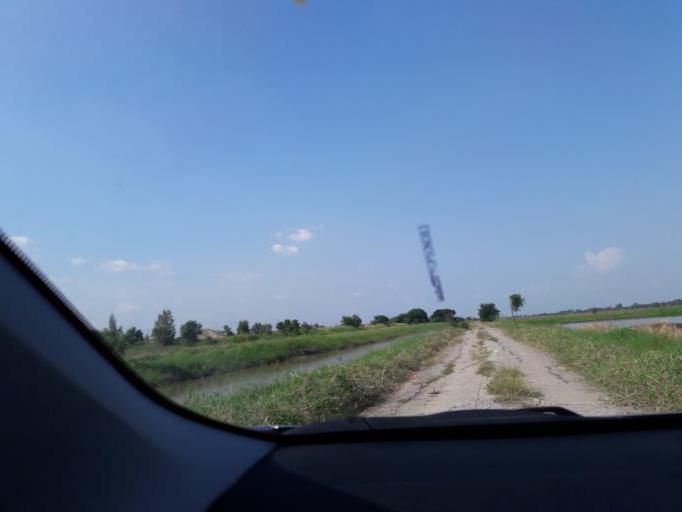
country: TH
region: Ang Thong
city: Ang Thong
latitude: 14.5513
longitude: 100.4066
